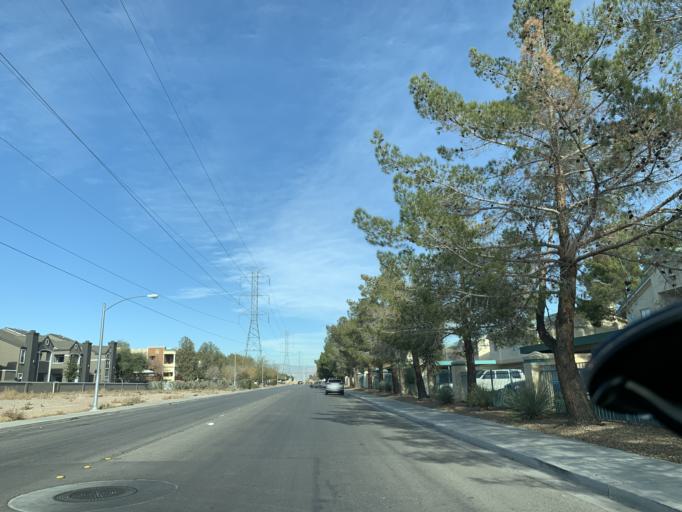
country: US
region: Nevada
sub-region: Clark County
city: Spring Valley
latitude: 36.0978
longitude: -115.2122
